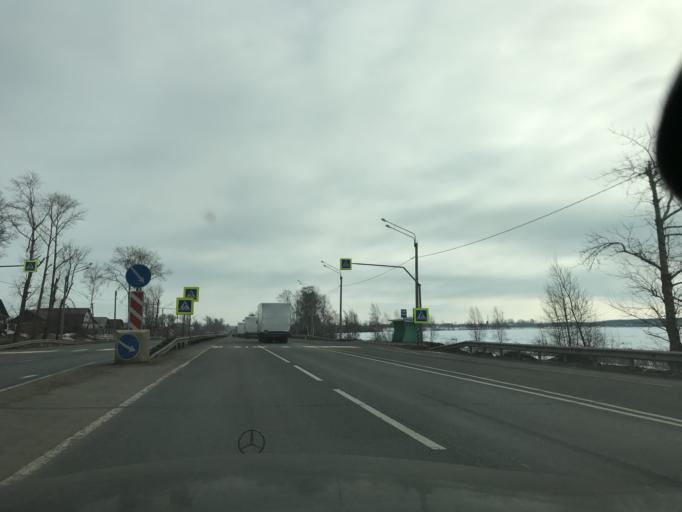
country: RU
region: Vladimir
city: Luknovo
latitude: 56.2392
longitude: 42.0711
